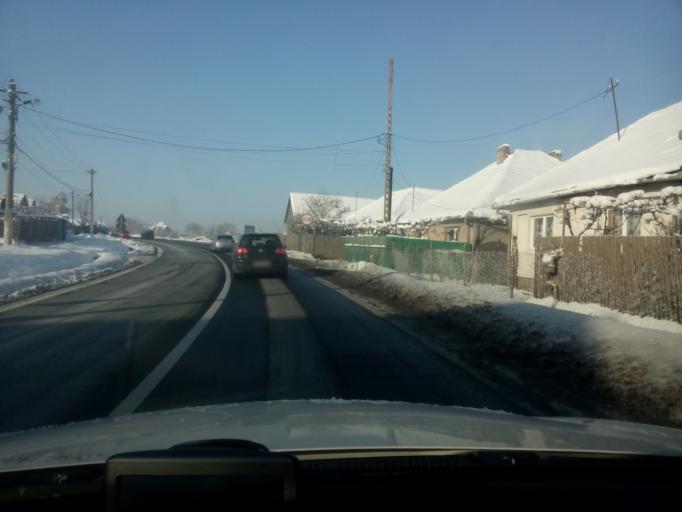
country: RO
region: Sibiu
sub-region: Comuna Talmaciu
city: Talmaciu
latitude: 45.6596
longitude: 24.2642
